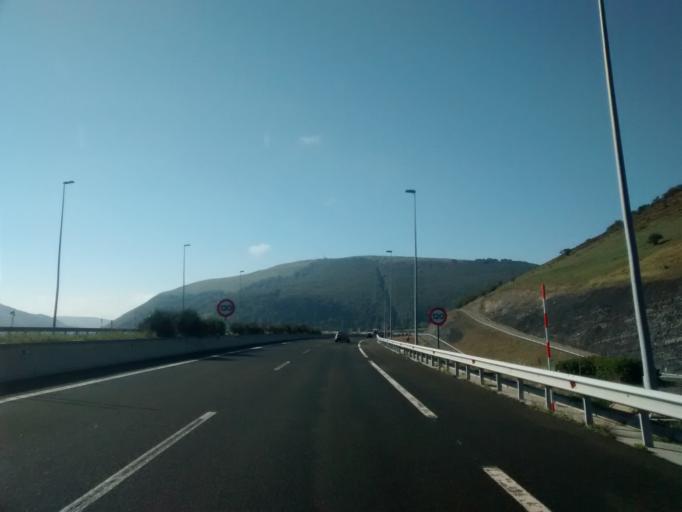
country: ES
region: Cantabria
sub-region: Provincia de Cantabria
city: Santiurde de Reinosa
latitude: 43.0693
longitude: -4.0866
